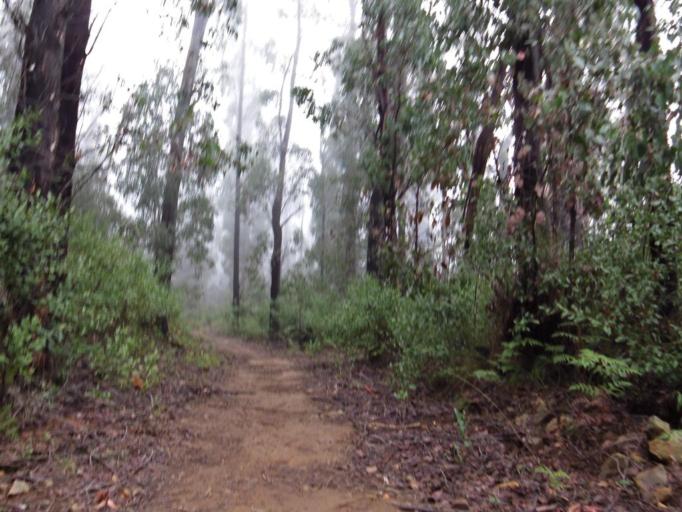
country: AU
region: Victoria
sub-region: Yarra Ranges
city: Millgrove
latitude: -37.5303
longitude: 145.7599
